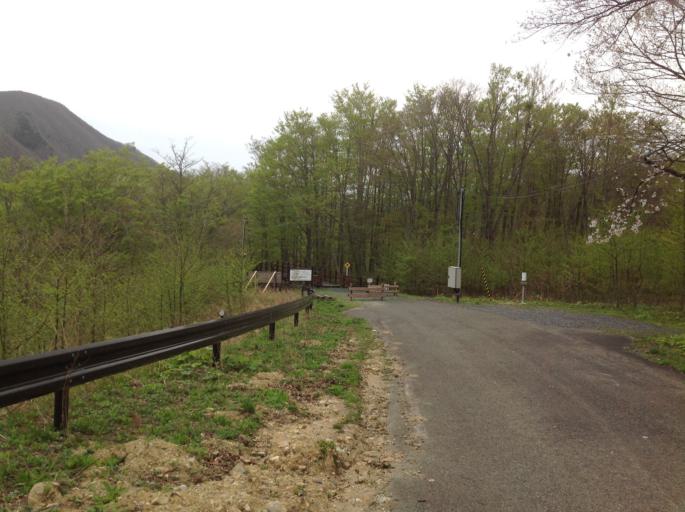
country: JP
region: Iwate
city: Ichinoseki
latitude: 39.0148
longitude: 140.8770
